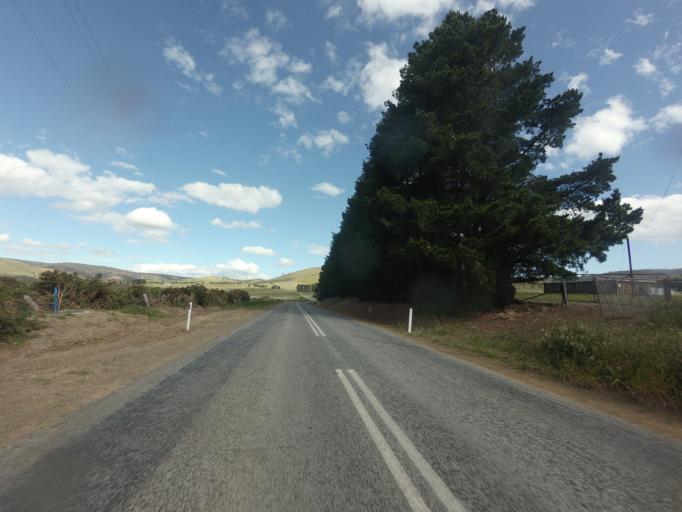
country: AU
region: Tasmania
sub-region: Brighton
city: Bridgewater
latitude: -42.5485
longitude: 147.3769
